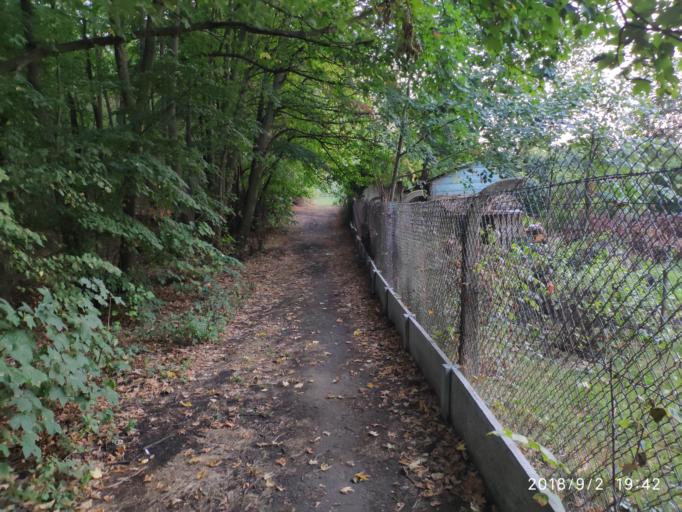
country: PL
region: Lubusz
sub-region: Zielona Gora
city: Zielona Gora
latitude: 51.9290
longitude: 15.5265
